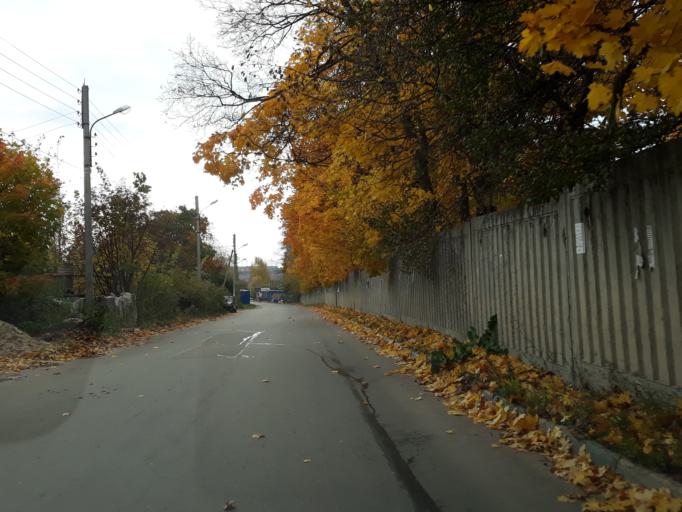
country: RU
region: Nizjnij Novgorod
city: Nizhniy Novgorod
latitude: 56.2357
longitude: 43.9776
